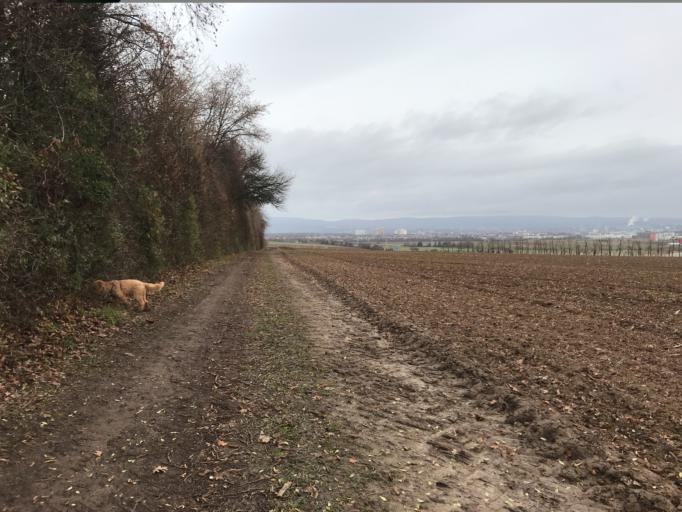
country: DE
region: Rheinland-Pfalz
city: Klein-Winternheim
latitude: 49.9682
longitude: 8.2132
